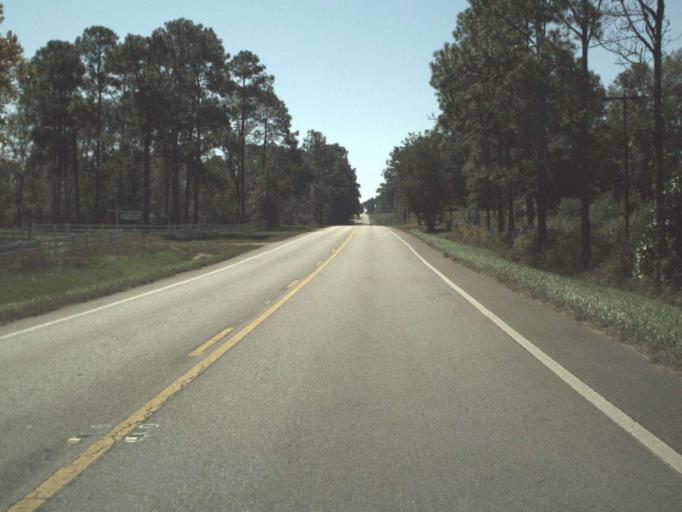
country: US
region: Alabama
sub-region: Geneva County
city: Samson
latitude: 30.9590
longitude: -86.1370
